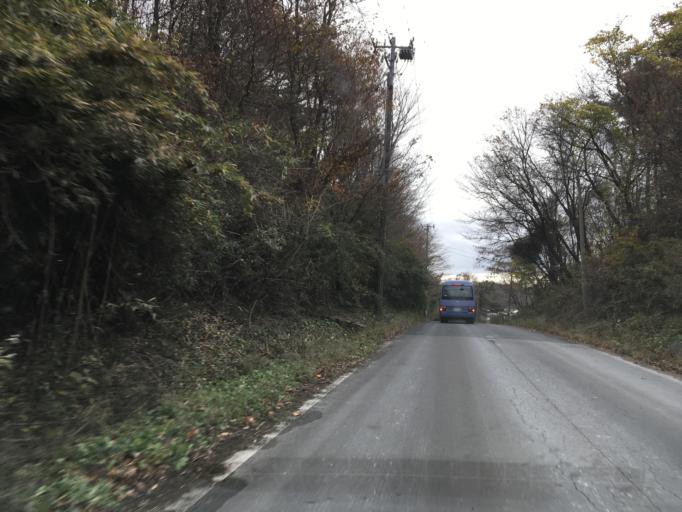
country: JP
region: Iwate
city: Ichinoseki
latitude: 38.8451
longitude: 141.0515
